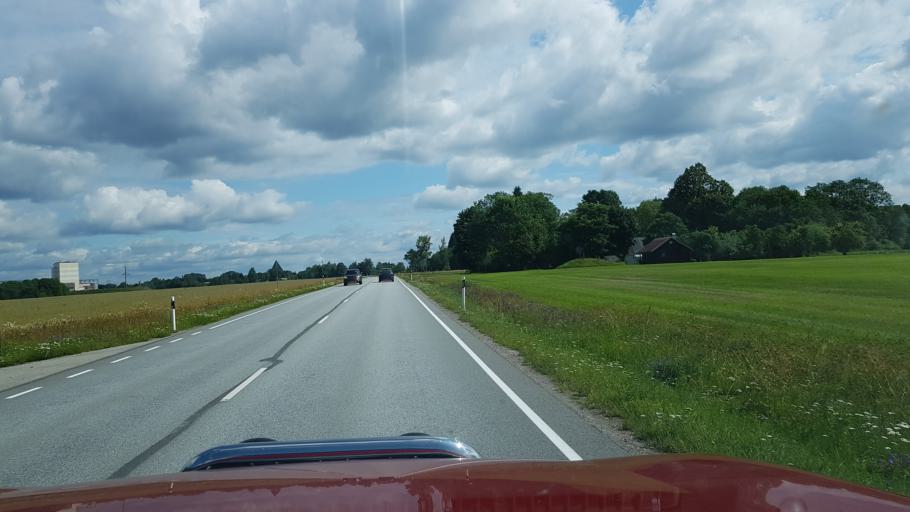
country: EE
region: Jogevamaa
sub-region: Jogeva linn
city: Jogeva
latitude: 58.8195
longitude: 26.5742
